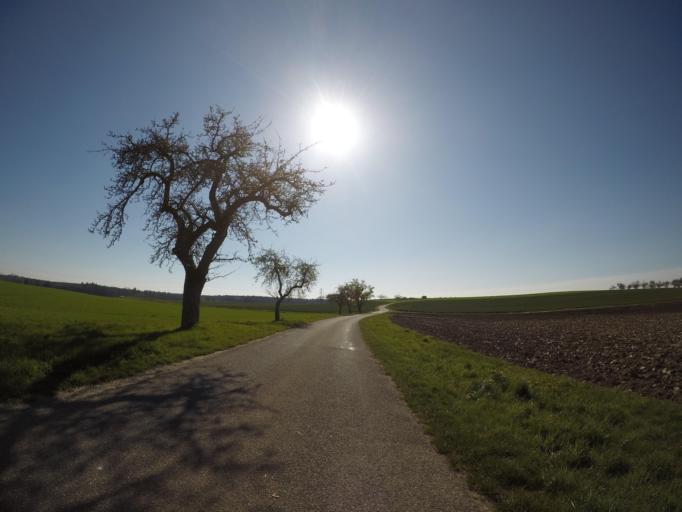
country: DE
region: Baden-Wuerttemberg
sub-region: Tuebingen Region
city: Ebenweiler
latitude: 47.8963
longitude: 9.5190
